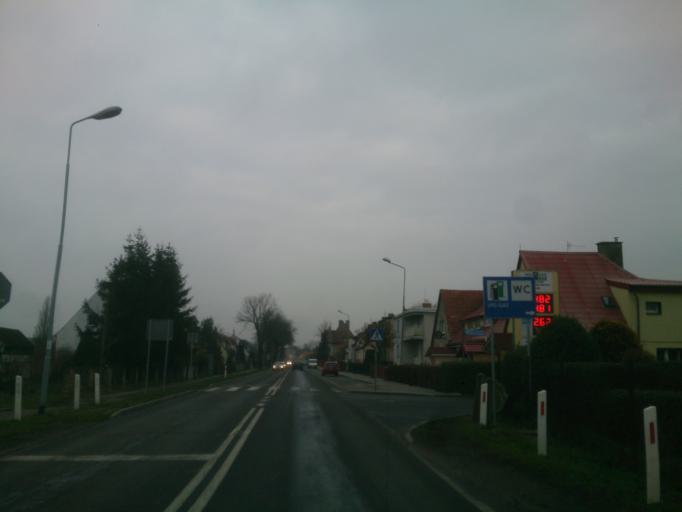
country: PL
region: West Pomeranian Voivodeship
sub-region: Powiat slawienski
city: Darlowo
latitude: 54.4123
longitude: 16.4105
